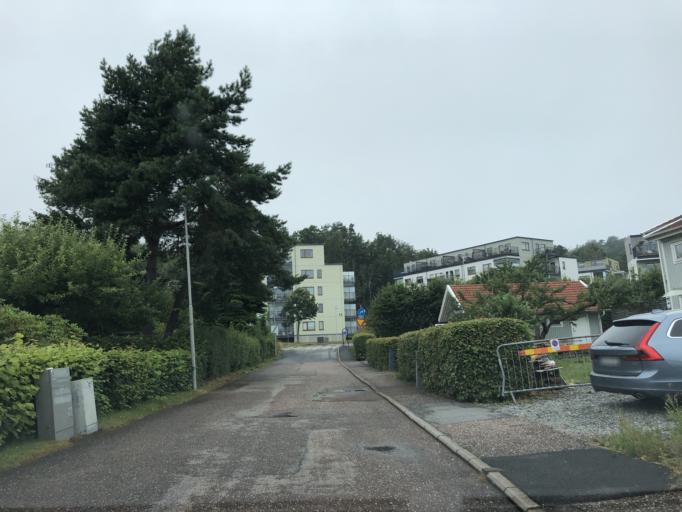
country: SE
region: Vaestra Goetaland
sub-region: Goteborg
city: Goeteborg
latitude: 57.7300
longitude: 11.9376
